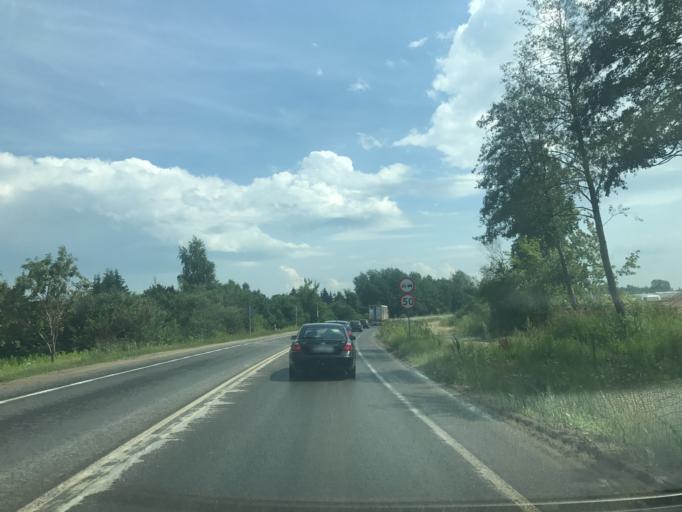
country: PL
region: Warmian-Masurian Voivodeship
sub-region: Powiat ostrodzki
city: Ostroda
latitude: 53.7121
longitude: 19.9722
